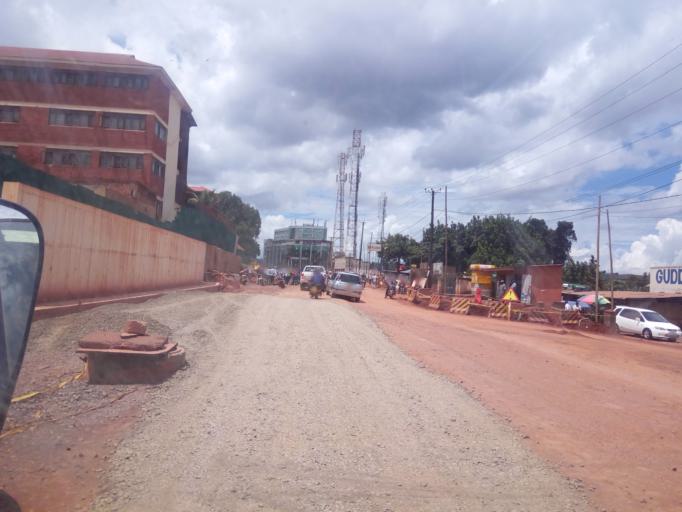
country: UG
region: Central Region
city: Kampala Central Division
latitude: 0.3279
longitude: 32.5688
